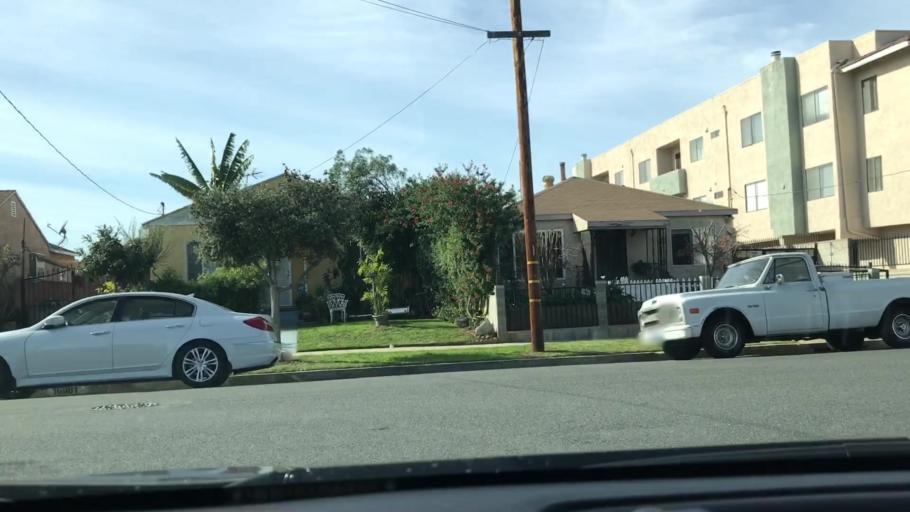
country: US
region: California
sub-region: Los Angeles County
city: Gardena
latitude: 33.8784
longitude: -118.3048
